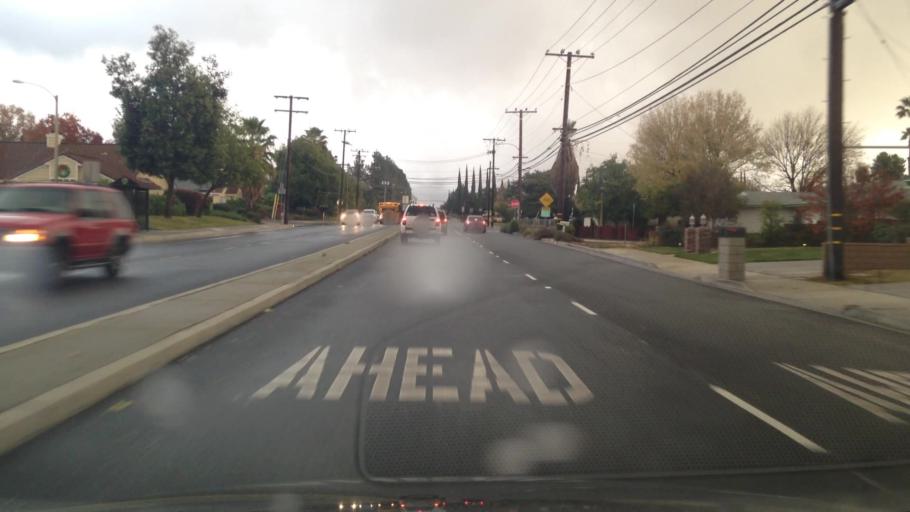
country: US
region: California
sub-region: Riverside County
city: Beaumont
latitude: 33.9470
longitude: -116.9729
